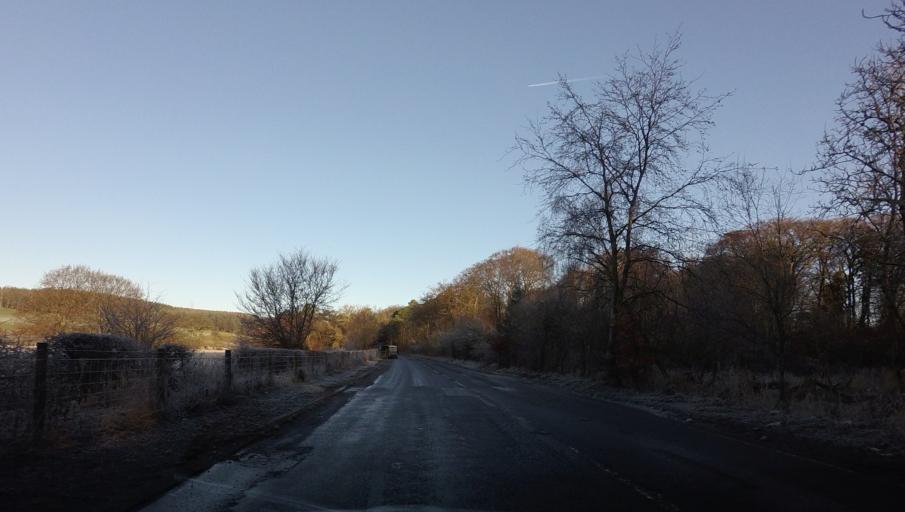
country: GB
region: Scotland
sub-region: North Lanarkshire
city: Newmains
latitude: 55.7965
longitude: -3.8507
